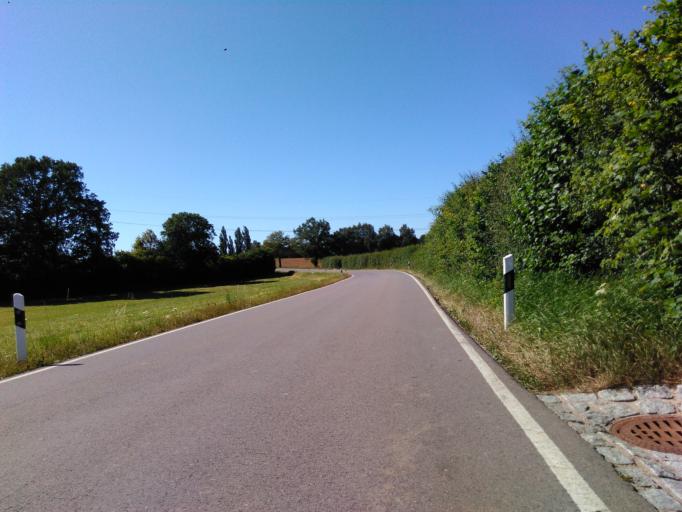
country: LU
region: Luxembourg
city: Schouweiler
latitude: 49.5717
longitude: 5.9661
